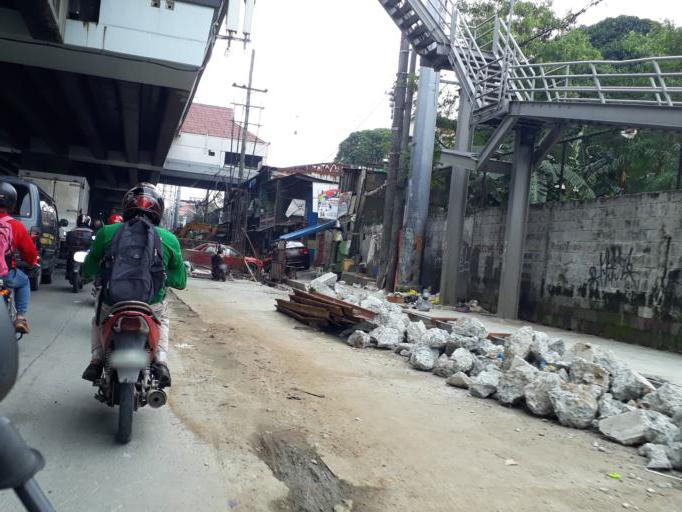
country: PH
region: Metro Manila
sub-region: City of Manila
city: Manila
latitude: 14.6354
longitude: 120.9821
